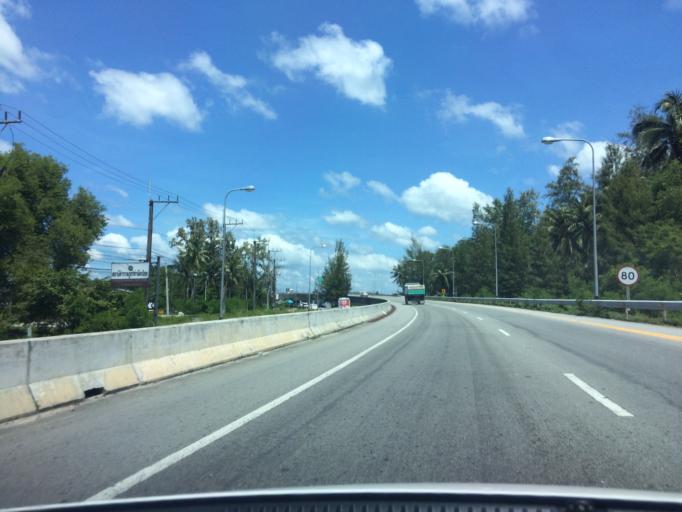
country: TH
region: Phuket
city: Thalang
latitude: 8.1970
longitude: 98.2958
